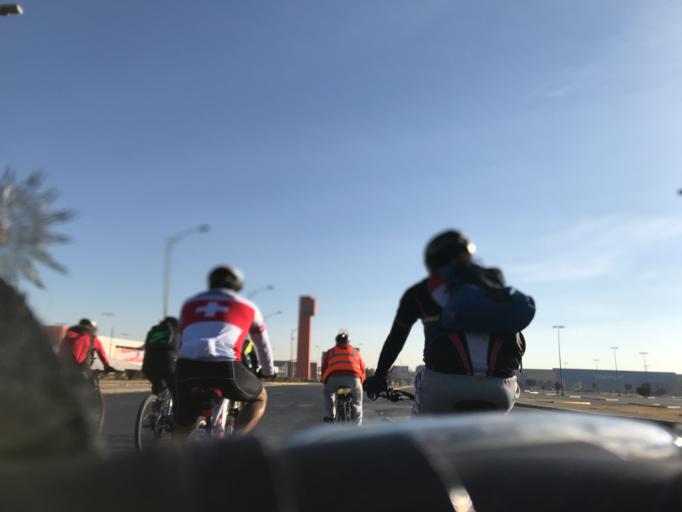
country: MX
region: Mexico
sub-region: Cuautitlan
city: La Trinidad
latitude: 19.6770
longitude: -99.1516
